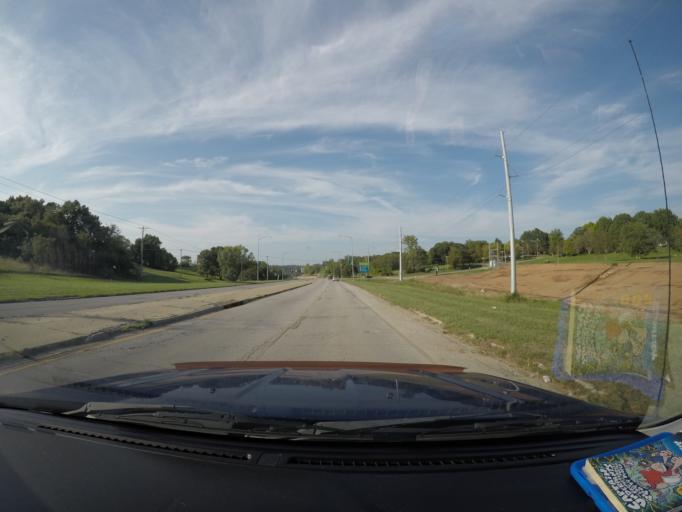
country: US
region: Kansas
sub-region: Atchison County
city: Atchison
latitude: 39.5456
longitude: -95.1298
